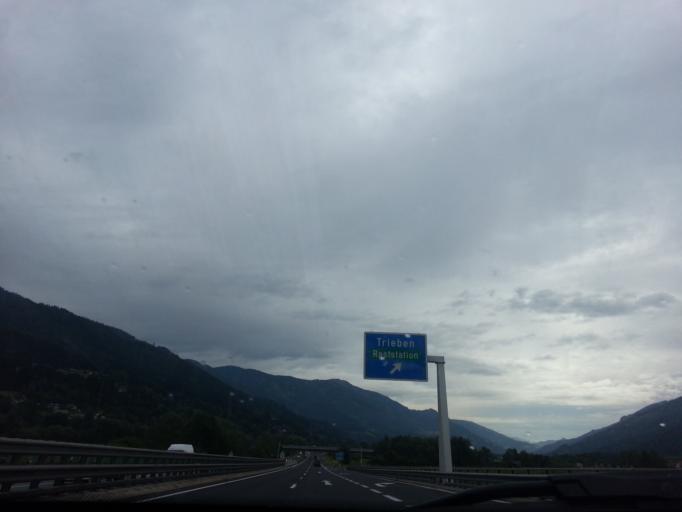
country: AT
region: Styria
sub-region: Politischer Bezirk Liezen
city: Trieben
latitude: 47.4965
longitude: 14.4784
